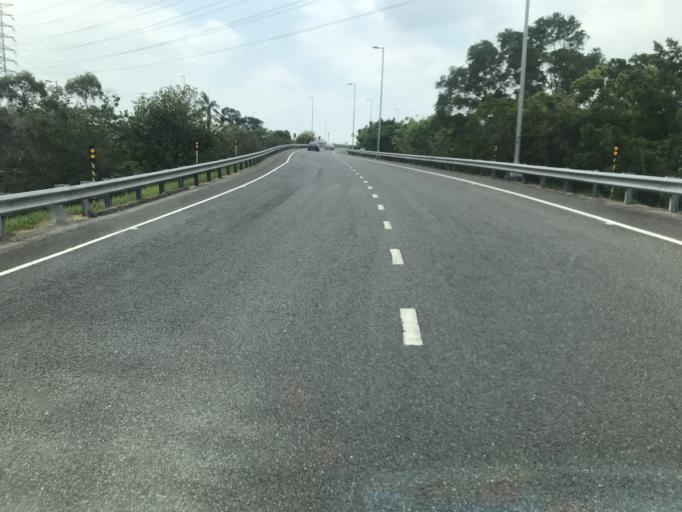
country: TW
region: Taiwan
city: Zhongxing New Village
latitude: 24.0054
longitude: 120.6508
